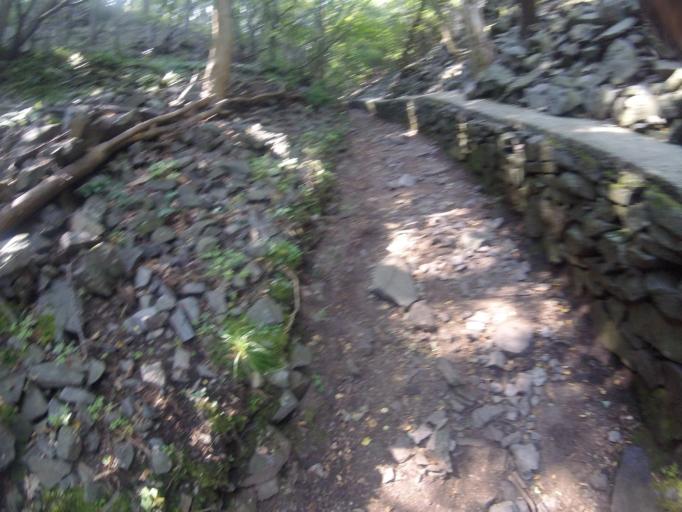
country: HU
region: Veszprem
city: Badacsonytomaj
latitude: 46.8062
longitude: 17.4944
